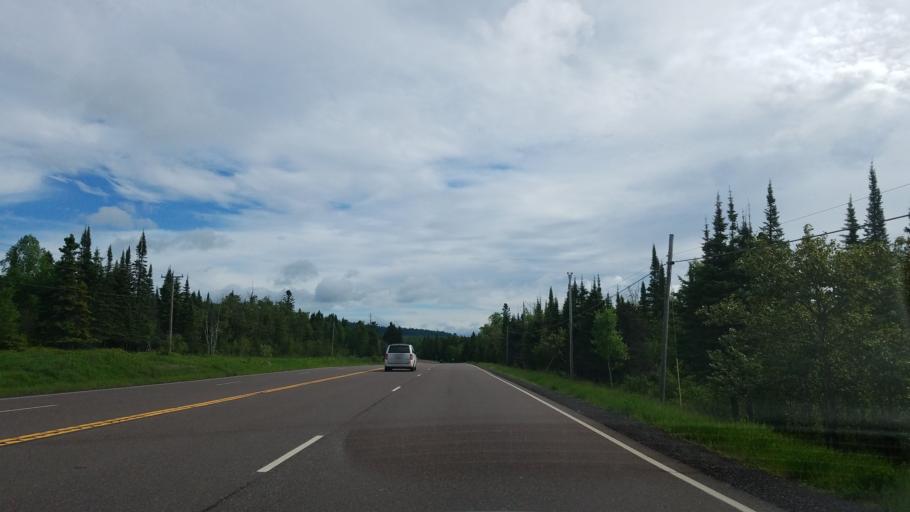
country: US
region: Minnesota
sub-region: Lake County
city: Two Harbors
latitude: 47.0823
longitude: -91.5832
